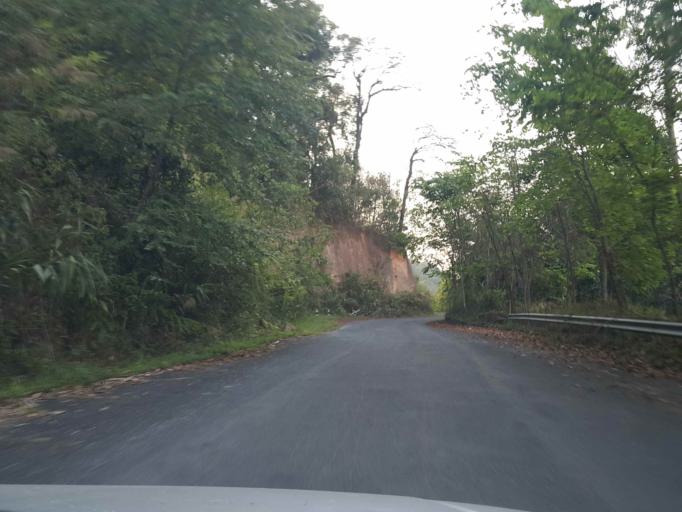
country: TH
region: Chiang Mai
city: Mae On
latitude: 19.0030
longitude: 99.3303
